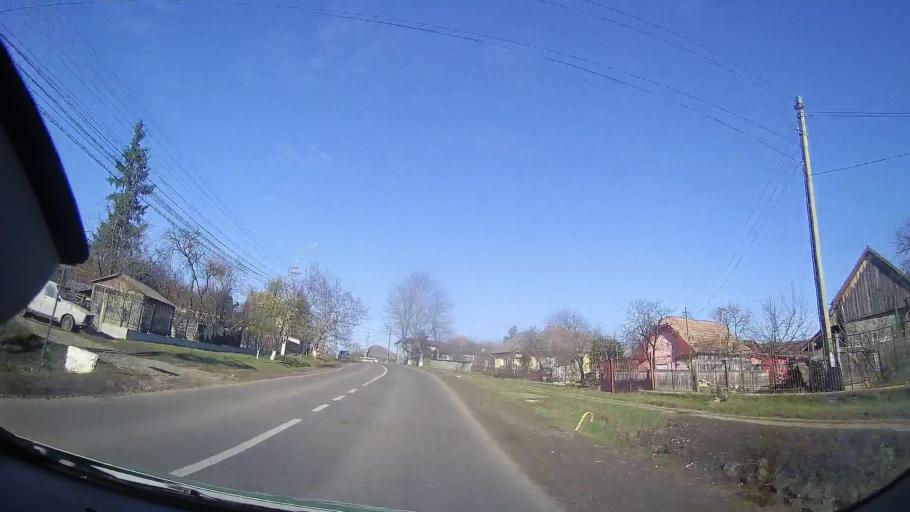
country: RO
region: Mures
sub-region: Comuna Mihesu de Campie
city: Mihesu de Campie
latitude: 46.6722
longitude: 24.1567
